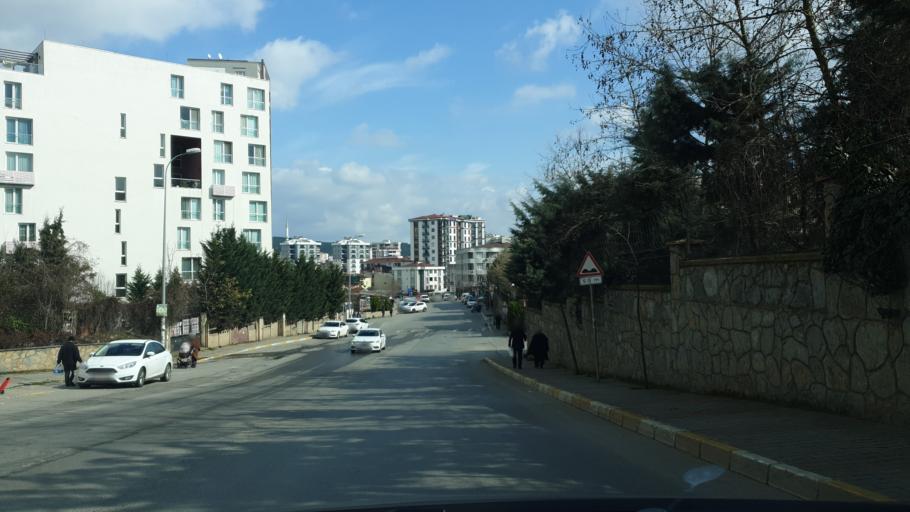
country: TR
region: Istanbul
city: Icmeler
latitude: 40.8696
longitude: 29.3199
